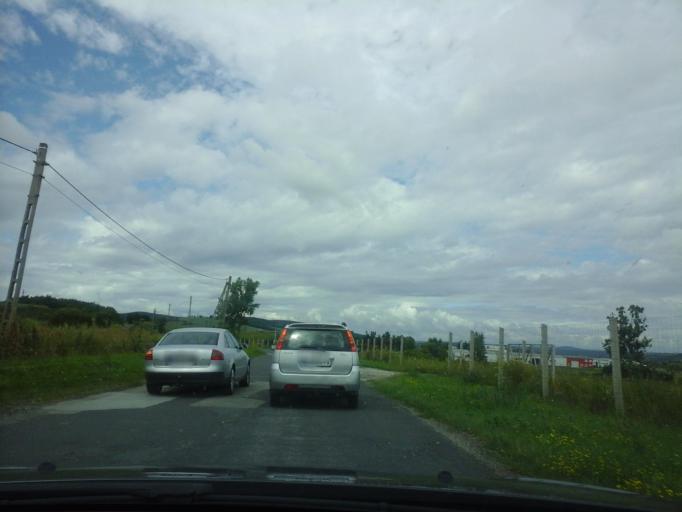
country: HU
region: Borsod-Abauj-Zemplen
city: Sajokaza
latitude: 48.3219
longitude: 20.6127
